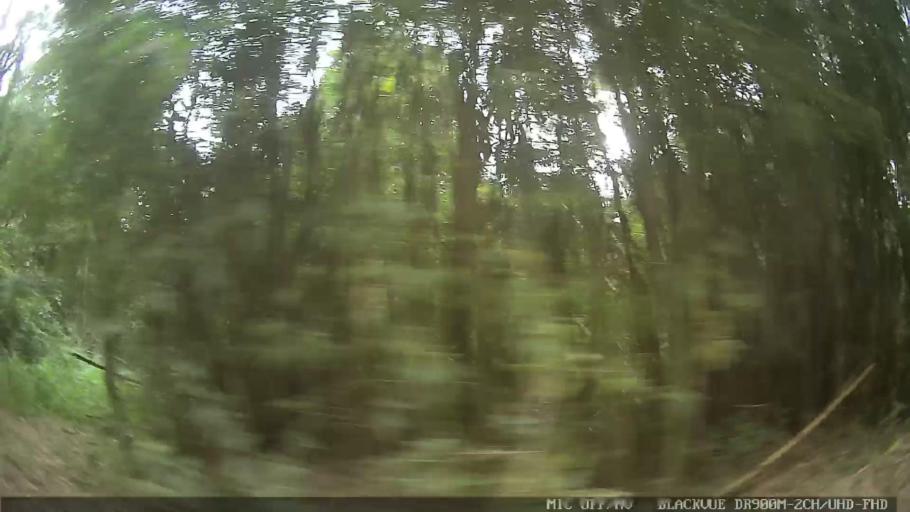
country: BR
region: Sao Paulo
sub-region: Bom Jesus Dos Perdoes
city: Bom Jesus dos Perdoes
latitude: -23.1460
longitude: -46.5065
